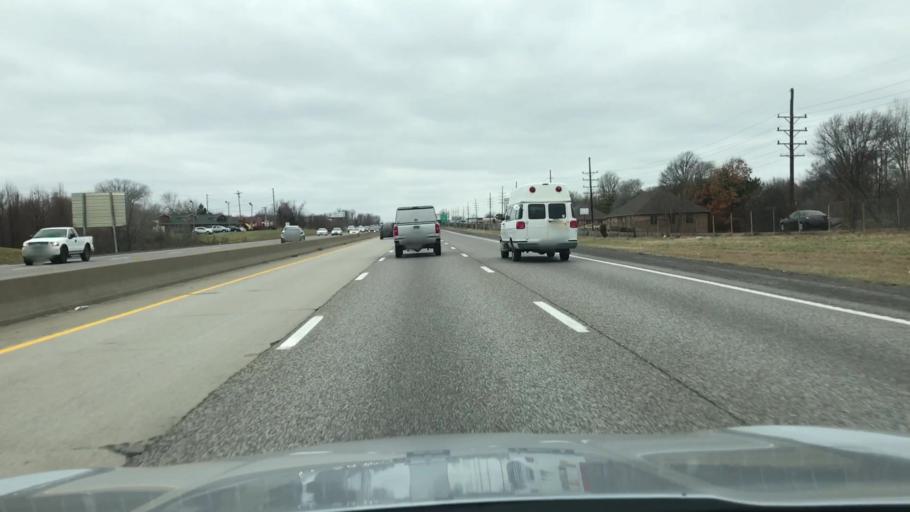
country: US
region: Missouri
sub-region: Saint Charles County
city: O'Fallon
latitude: 38.8026
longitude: -90.7101
